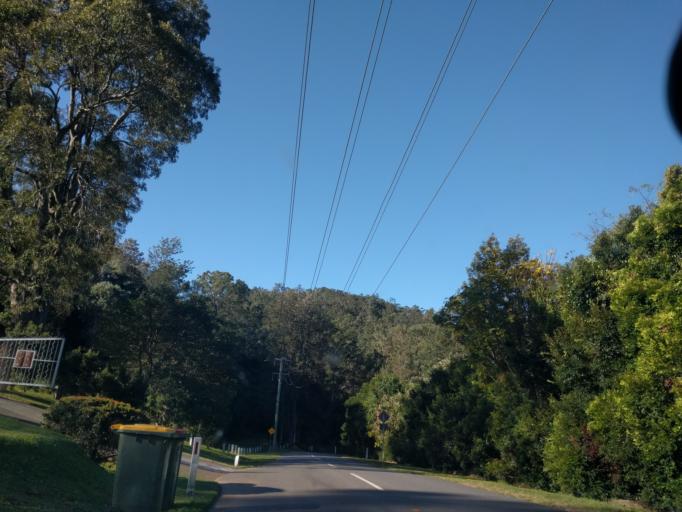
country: AU
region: Queensland
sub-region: Brisbane
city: Pullenvale
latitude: -27.4712
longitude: 152.8491
